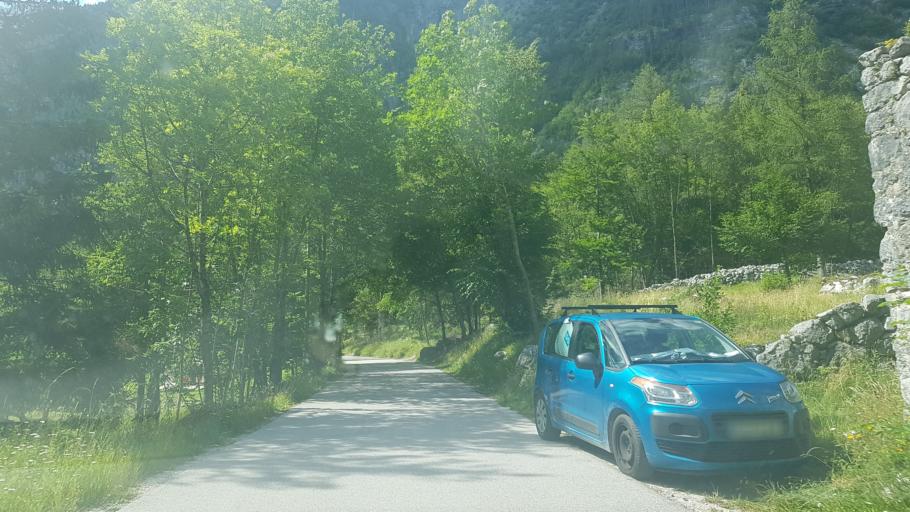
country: SI
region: Kranjska Gora
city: Kranjska Gora
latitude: 46.4085
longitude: 13.7271
